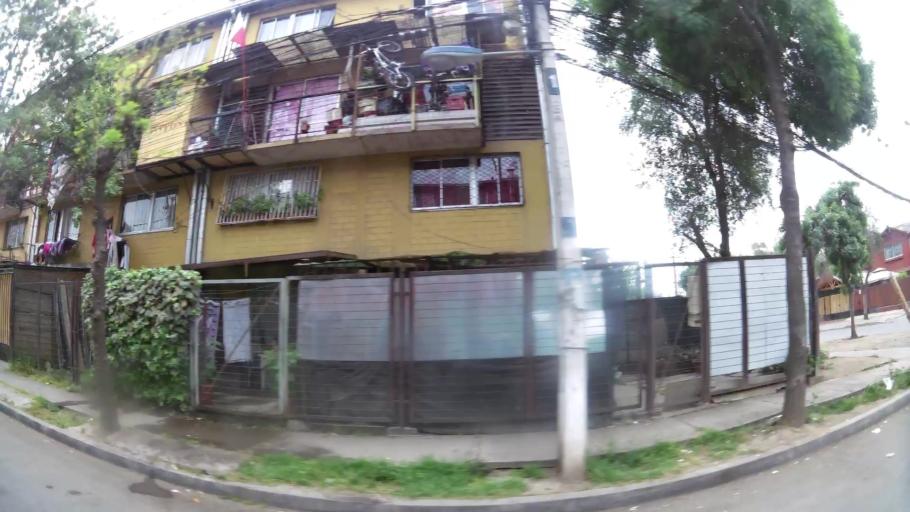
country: CL
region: Santiago Metropolitan
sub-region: Provincia de Santiago
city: Villa Presidente Frei, Nunoa, Santiago, Chile
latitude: -33.4961
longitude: -70.5894
